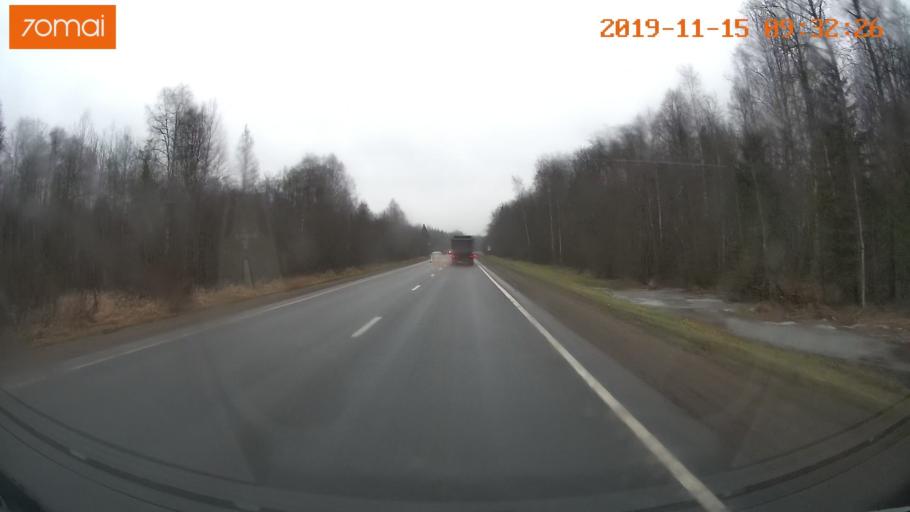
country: RU
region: Vologda
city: Sheksna
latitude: 59.2716
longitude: 38.3350
